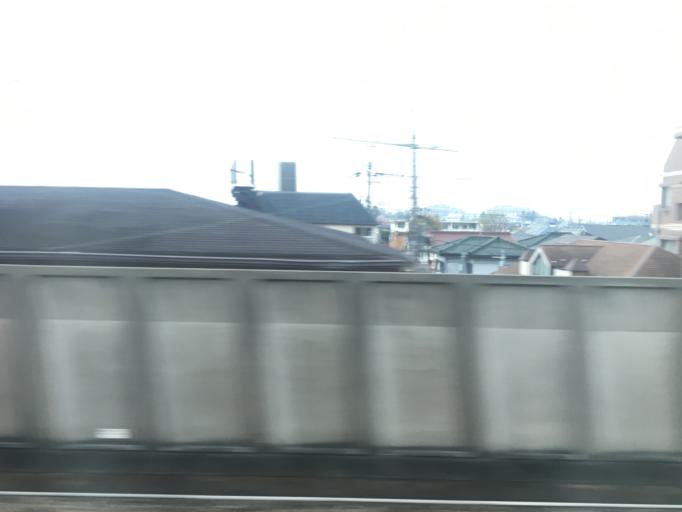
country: JP
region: Tokyo
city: Hino
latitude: 35.6988
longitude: 139.4335
